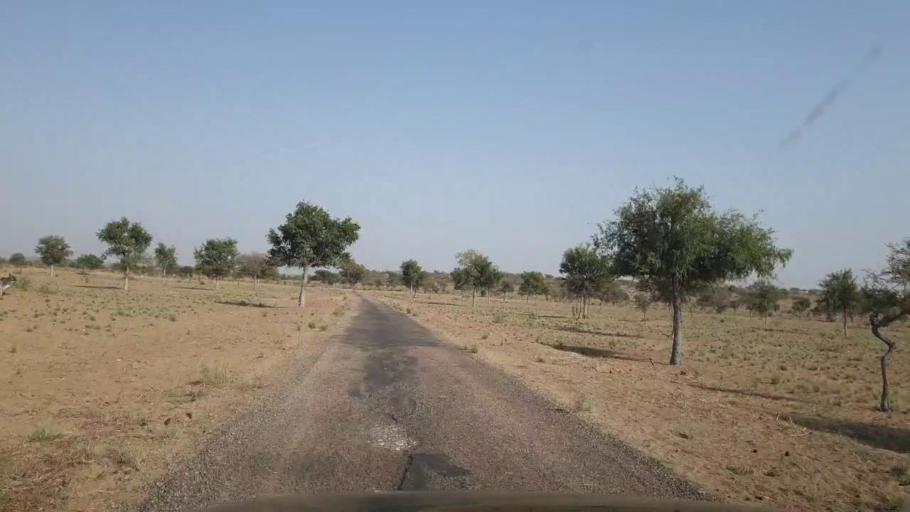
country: PK
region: Sindh
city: Islamkot
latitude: 25.1306
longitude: 70.4862
